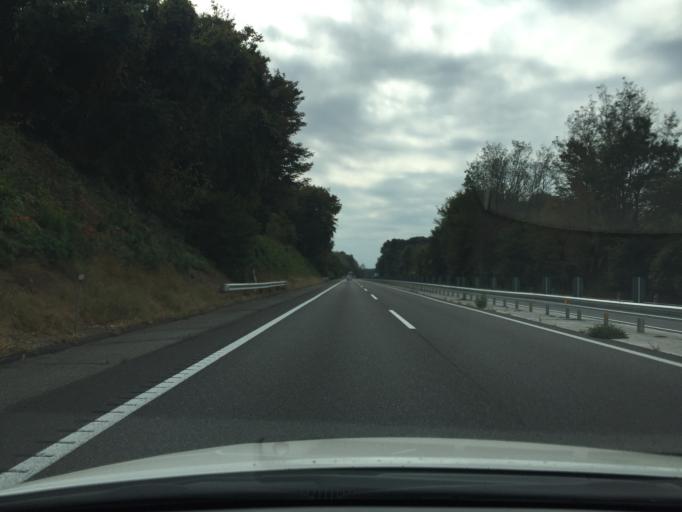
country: JP
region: Fukushima
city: Sukagawa
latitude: 37.2388
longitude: 140.3282
